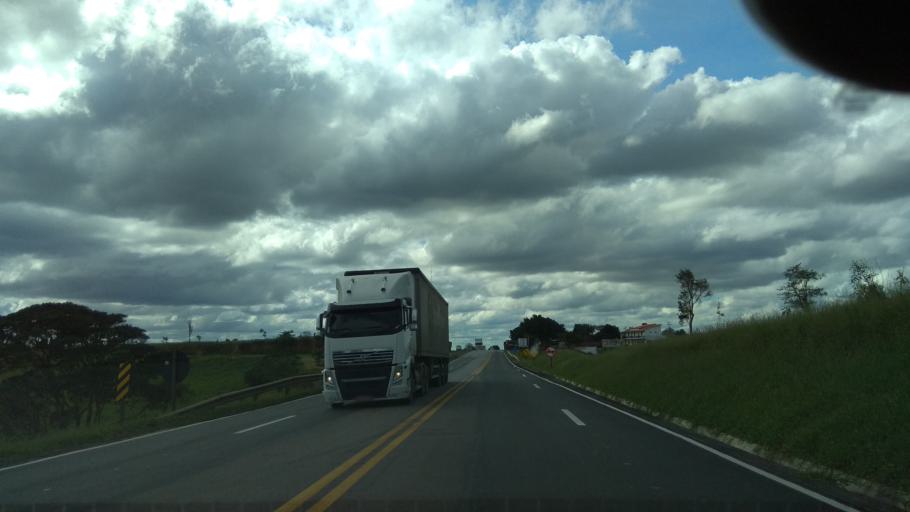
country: BR
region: Bahia
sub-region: Santa Ines
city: Santa Ines
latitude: -13.0995
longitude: -39.9637
